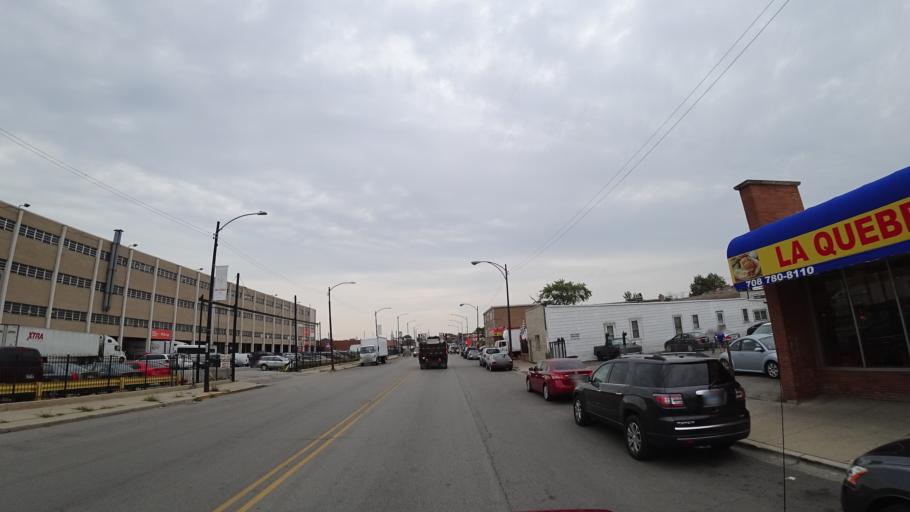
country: US
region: Illinois
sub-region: Cook County
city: Cicero
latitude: 41.8659
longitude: -87.7471
